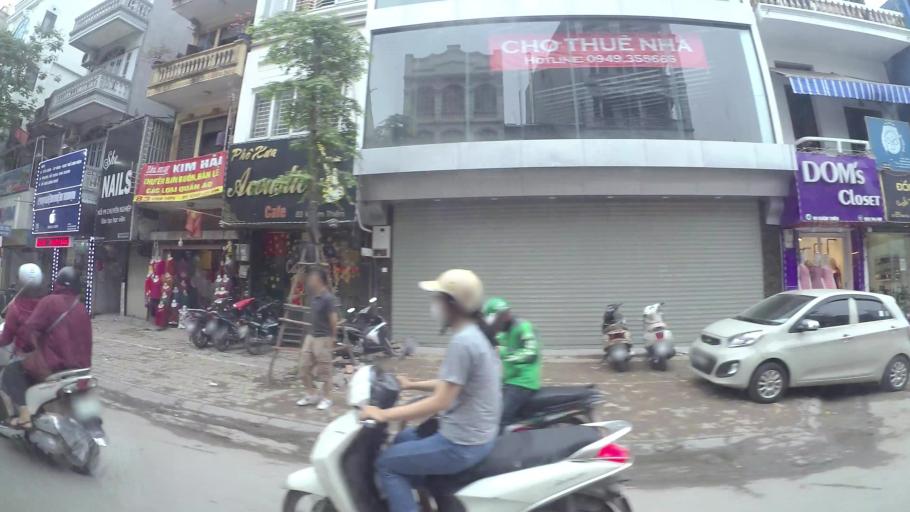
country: VN
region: Ha Noi
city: Hanoi
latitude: 21.0190
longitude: 105.8377
